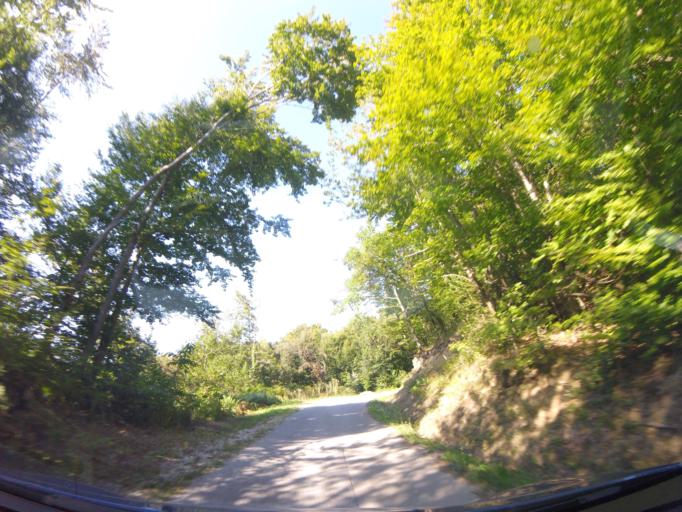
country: HR
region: Zagrebacka
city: Rude
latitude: 45.7560
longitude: 15.6690
